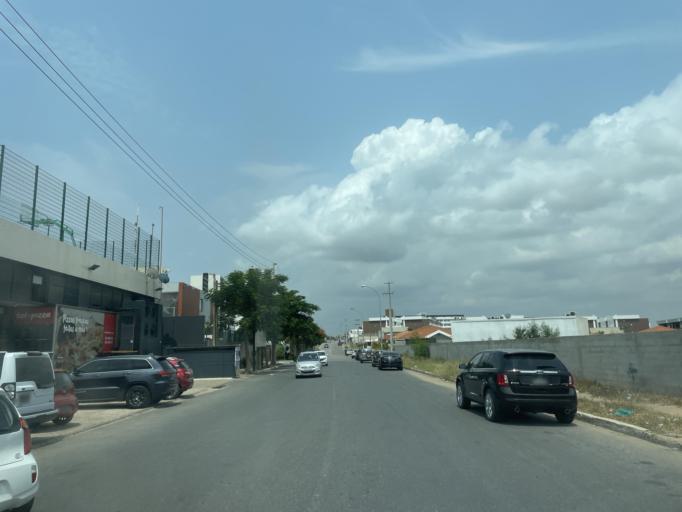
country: AO
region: Luanda
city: Luanda
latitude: -8.9234
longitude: 13.1988
